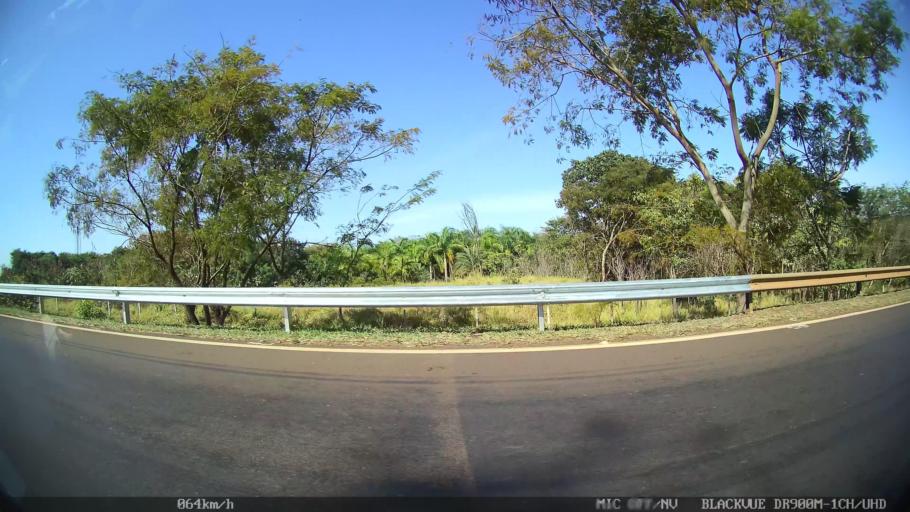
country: BR
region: Sao Paulo
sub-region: Batatais
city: Batatais
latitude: -20.9021
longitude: -47.6059
